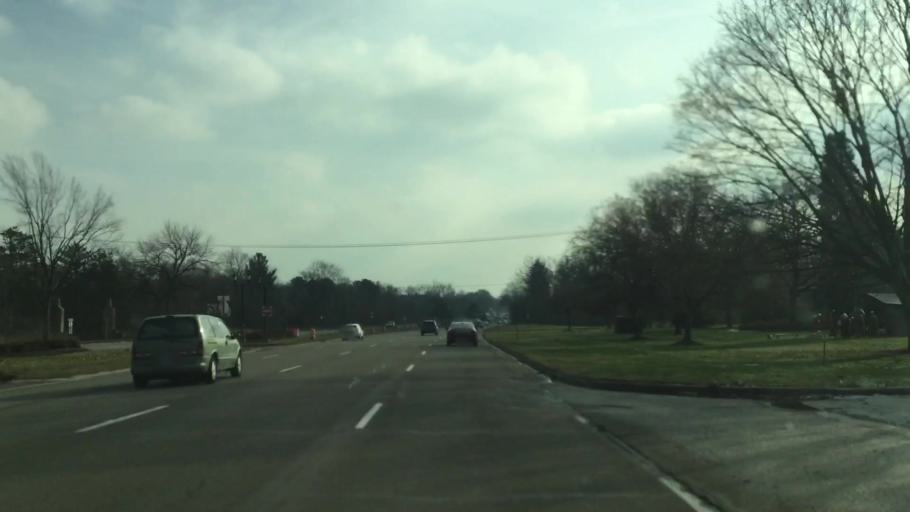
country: US
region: Michigan
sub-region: Oakland County
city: Bloomfield Hills
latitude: 42.5663
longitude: -83.2292
